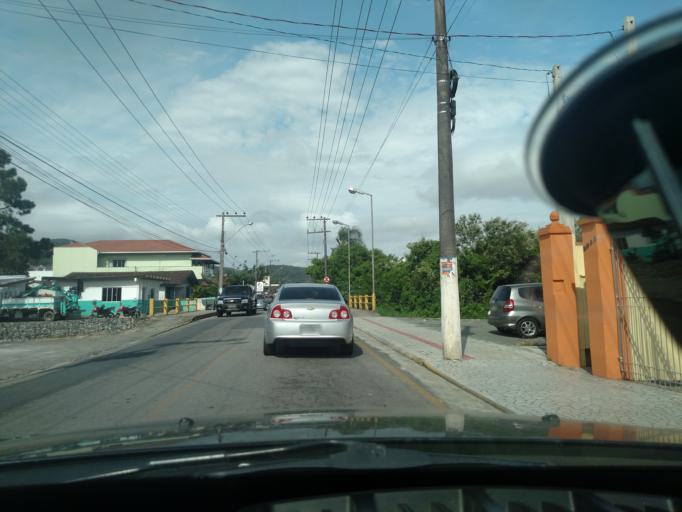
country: BR
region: Santa Catarina
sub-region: Porto Belo
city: Porto Belo
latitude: -27.1530
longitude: -48.5391
